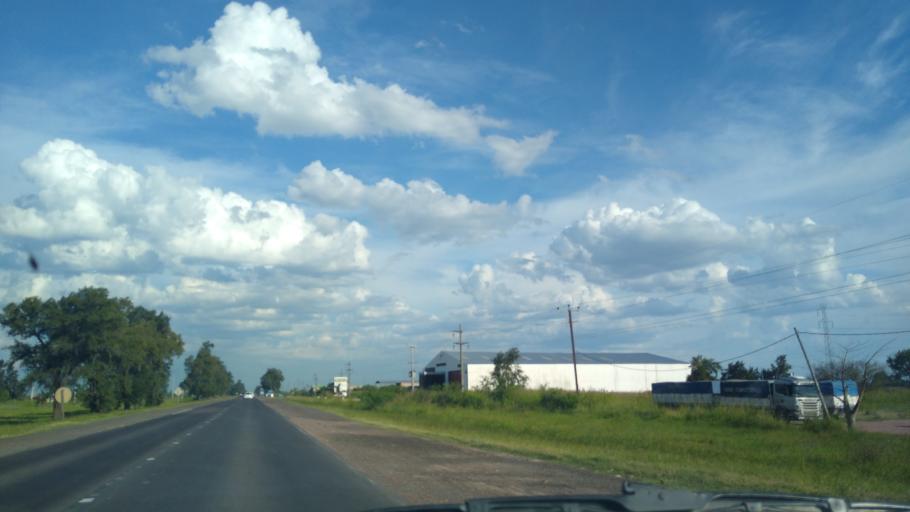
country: AR
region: Chaco
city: Presidencia Roque Saenz Pena
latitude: -26.8157
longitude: -60.4094
